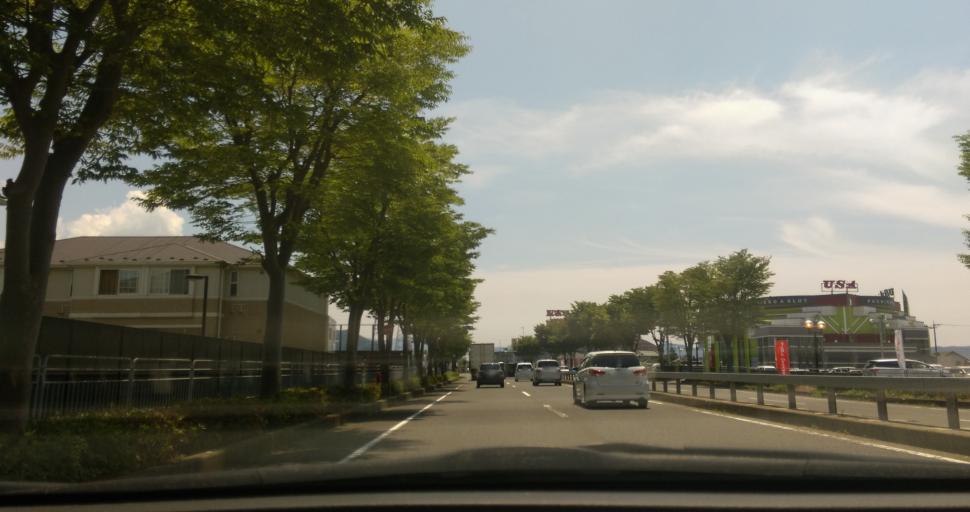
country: JP
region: Fukui
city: Sabae
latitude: 35.9376
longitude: 136.1910
